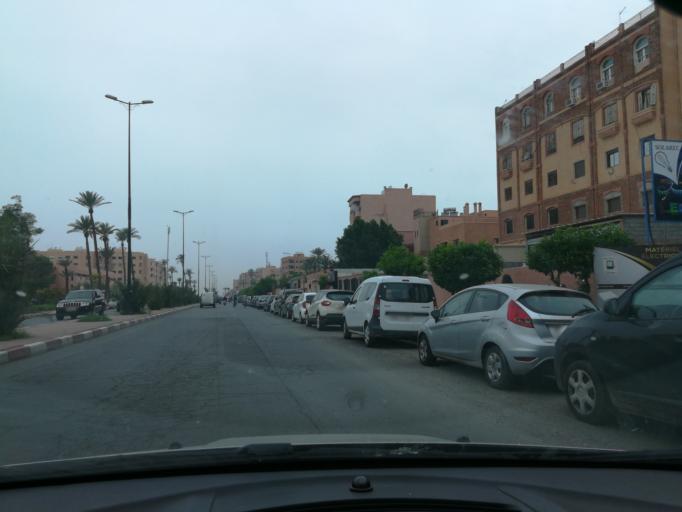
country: MA
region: Marrakech-Tensift-Al Haouz
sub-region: Marrakech
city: Marrakesh
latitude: 31.6499
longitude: -8.0146
